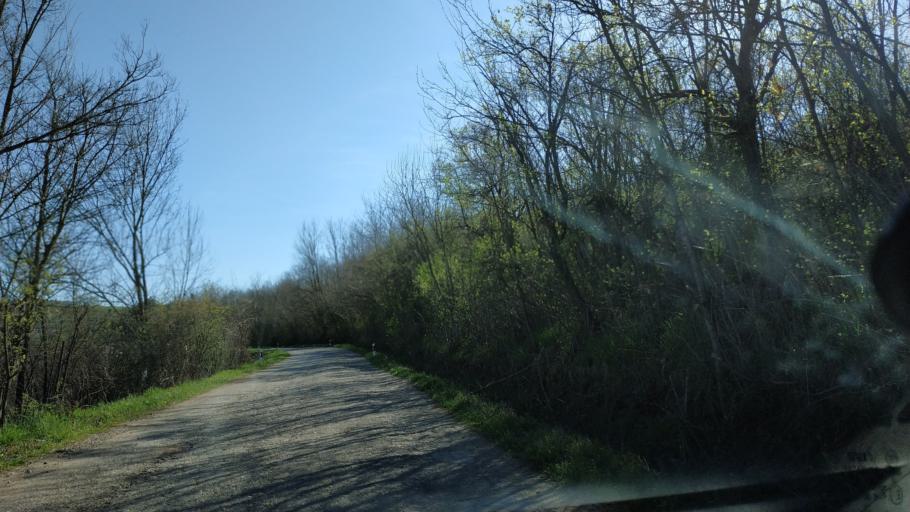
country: RS
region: Central Serbia
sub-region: Nisavski Okrug
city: Aleksinac
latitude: 43.4797
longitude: 21.6526
